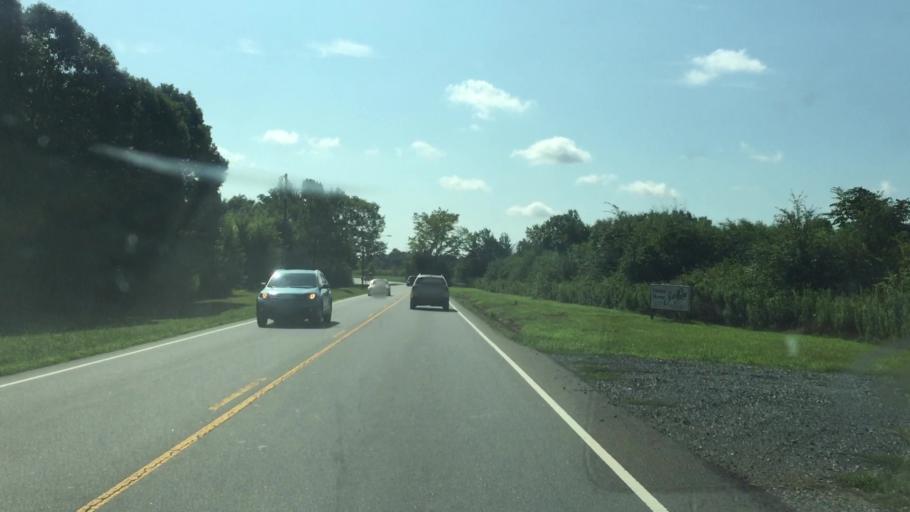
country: US
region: North Carolina
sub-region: Mecklenburg County
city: Mint Hill
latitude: 35.1734
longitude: -80.6192
